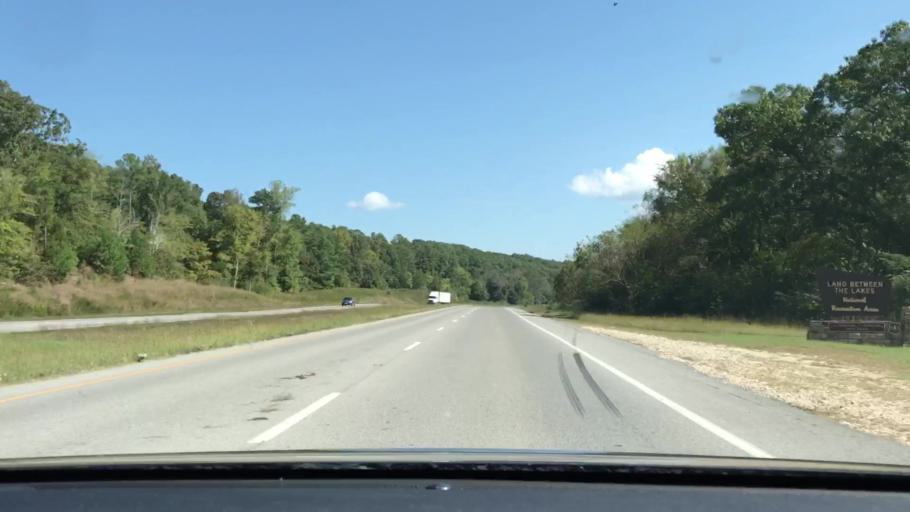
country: US
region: Kentucky
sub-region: Marshall County
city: Benton
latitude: 36.7772
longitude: -88.1015
